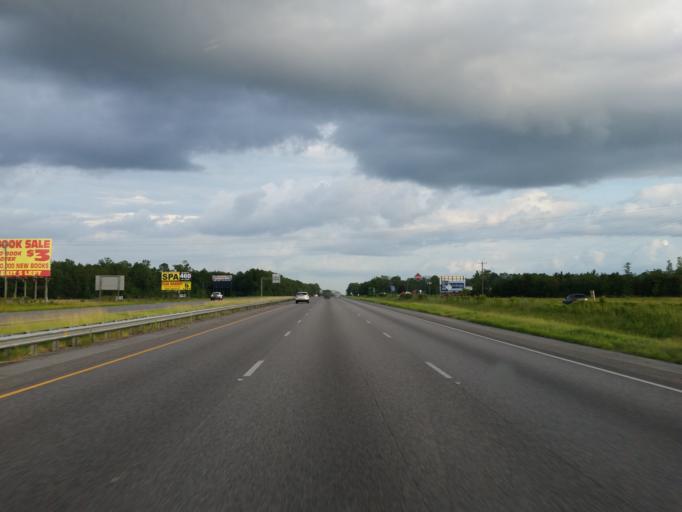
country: US
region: Georgia
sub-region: Lowndes County
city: Valdosta
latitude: 30.7455
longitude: -83.2704
